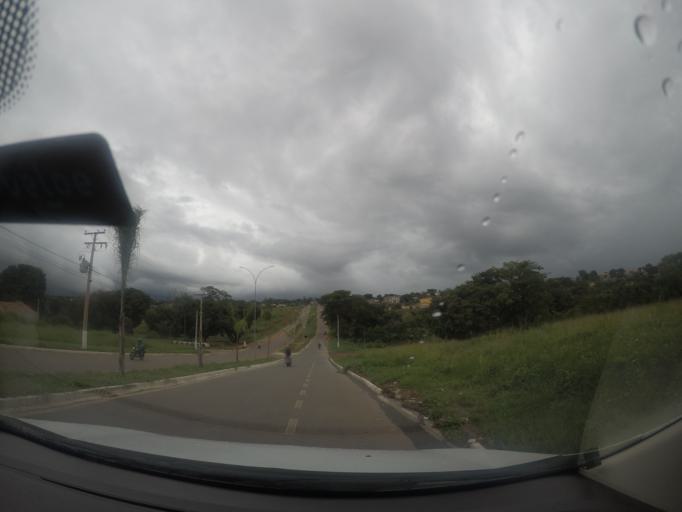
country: BR
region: Goias
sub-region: Trindade
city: Trindade
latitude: -16.6277
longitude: -49.3891
